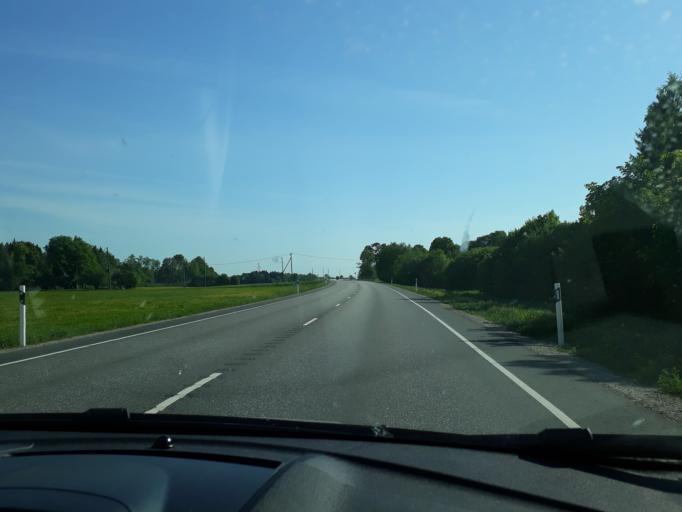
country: EE
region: Paernumaa
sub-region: Tootsi vald
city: Tootsi
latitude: 58.5692
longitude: 24.8750
